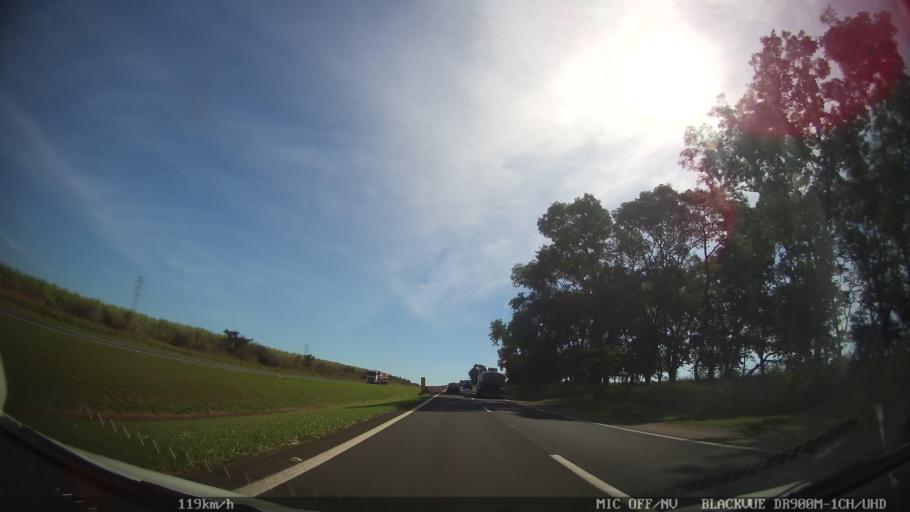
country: BR
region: Sao Paulo
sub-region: Porto Ferreira
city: Porto Ferreira
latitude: -21.8911
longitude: -47.4822
